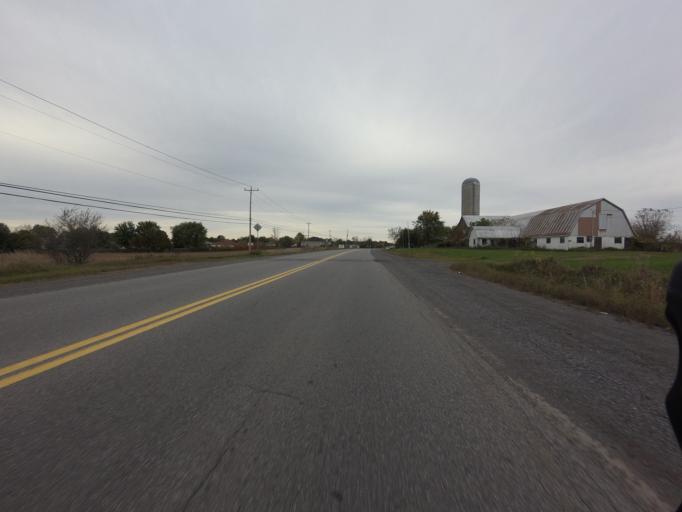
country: CA
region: Ontario
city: Bells Corners
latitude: 45.1394
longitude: -75.7146
